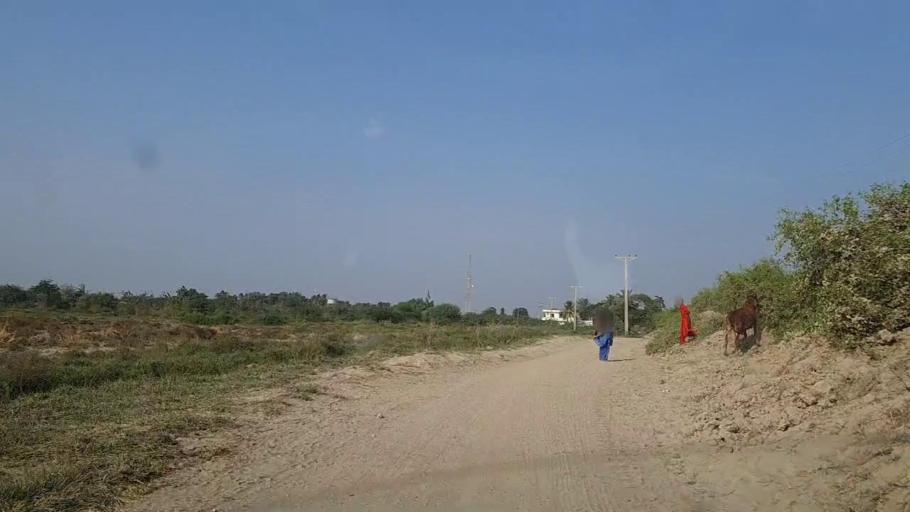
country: PK
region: Sindh
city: Mirpur Sakro
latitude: 24.5880
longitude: 67.5686
